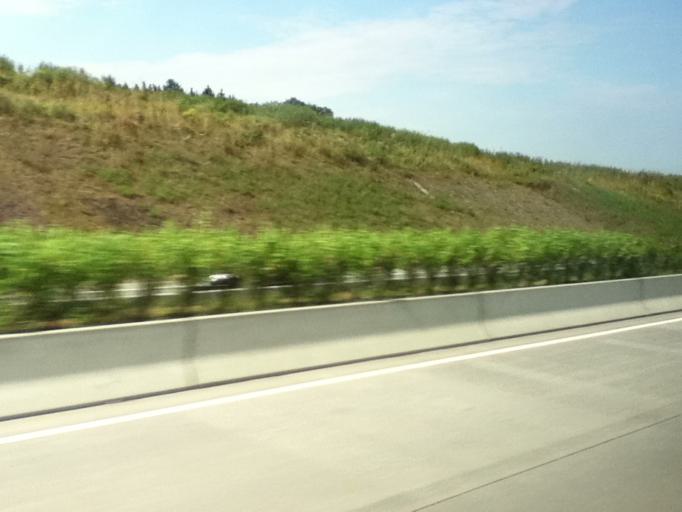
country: DE
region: Thuringia
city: Nobdenitz
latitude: 50.8657
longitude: 12.2750
